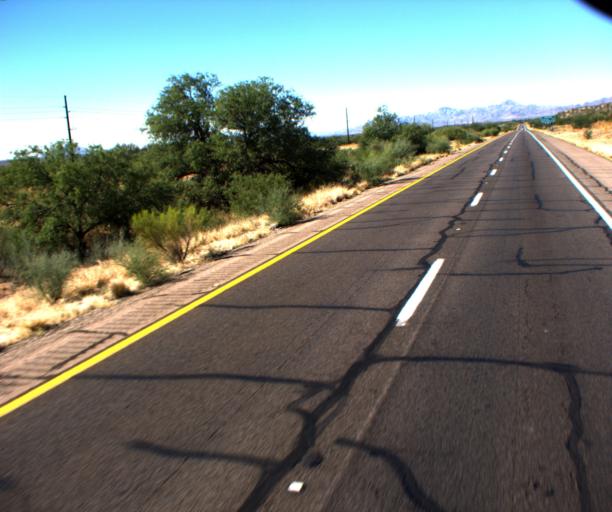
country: US
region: Arizona
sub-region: Pima County
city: Arivaca Junction
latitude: 31.7571
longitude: -111.0406
